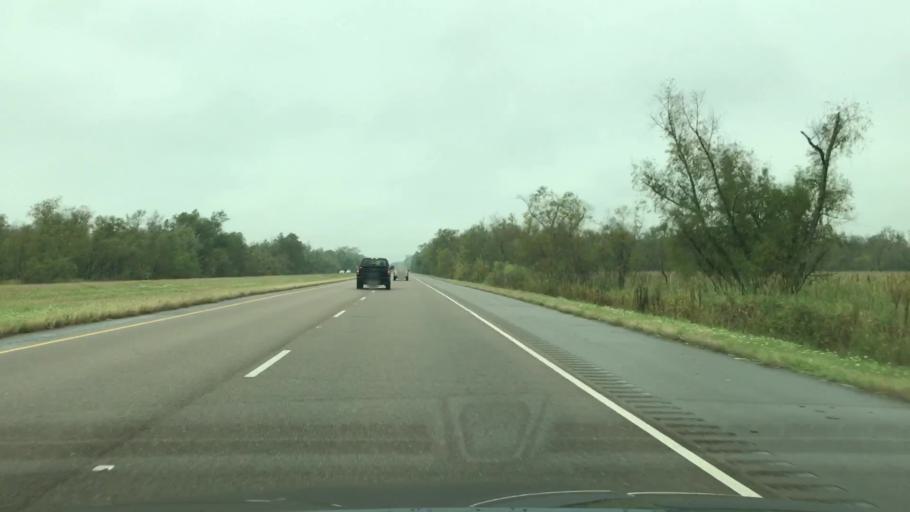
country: US
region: Louisiana
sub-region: Terrebonne Parish
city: Bayou Cane
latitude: 29.6877
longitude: -90.6894
